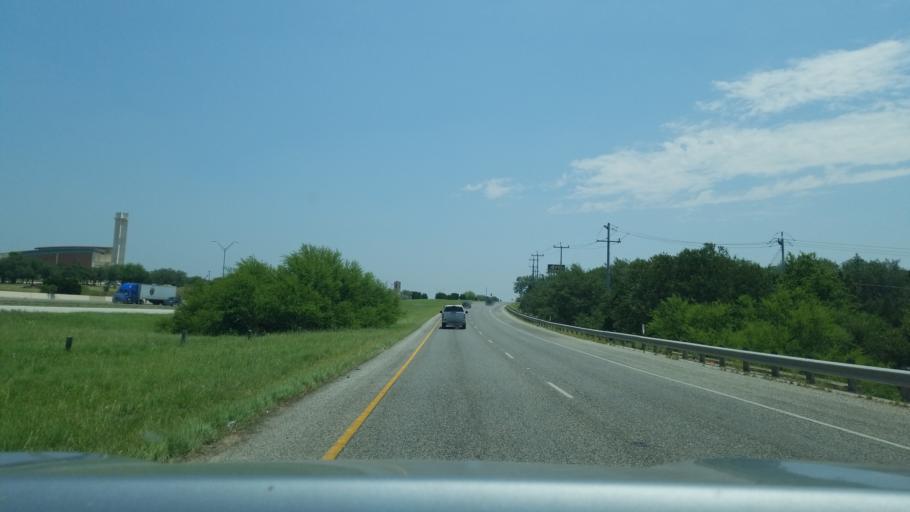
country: US
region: Texas
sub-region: Bexar County
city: Shavano Park
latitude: 29.6060
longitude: -98.5277
